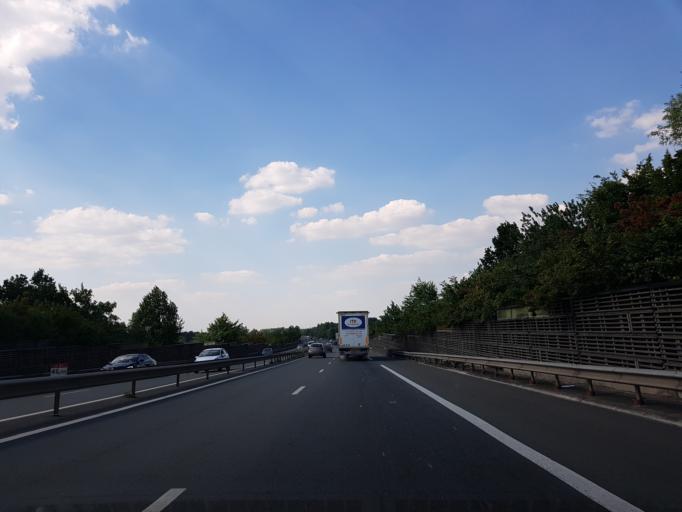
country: FR
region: Nord-Pas-de-Calais
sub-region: Departement du Nord
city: Somain
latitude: 50.3578
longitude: 3.2628
